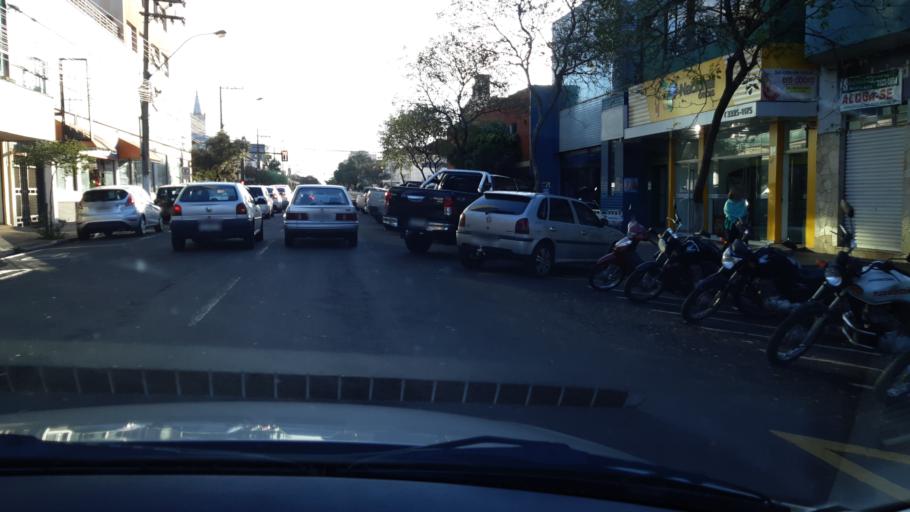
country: BR
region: Sao Paulo
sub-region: Ourinhos
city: Ourinhos
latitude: -22.9788
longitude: -49.8673
